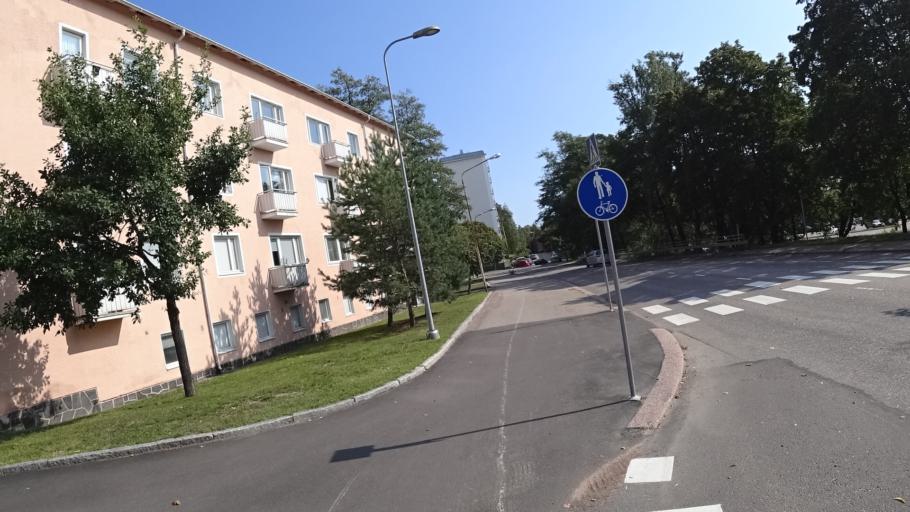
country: FI
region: Kymenlaakso
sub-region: Kotka-Hamina
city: Kotka
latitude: 60.4581
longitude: 26.9299
